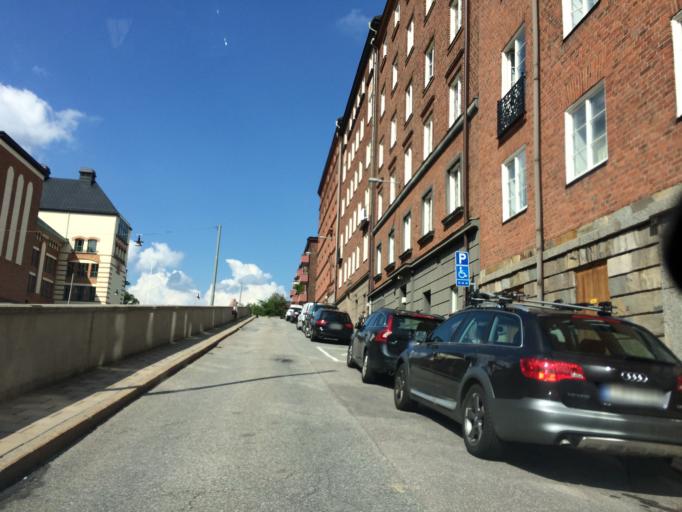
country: SE
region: Stockholm
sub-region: Stockholms Kommun
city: Stockholm
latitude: 59.3302
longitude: 18.0359
